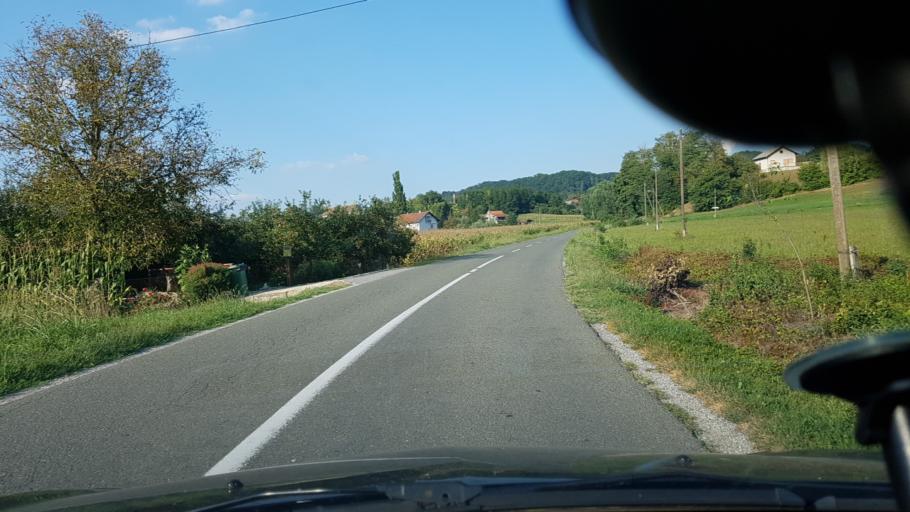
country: SI
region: Bistrica ob Sotli
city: Bistrica ob Sotli
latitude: 46.0207
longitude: 15.7260
